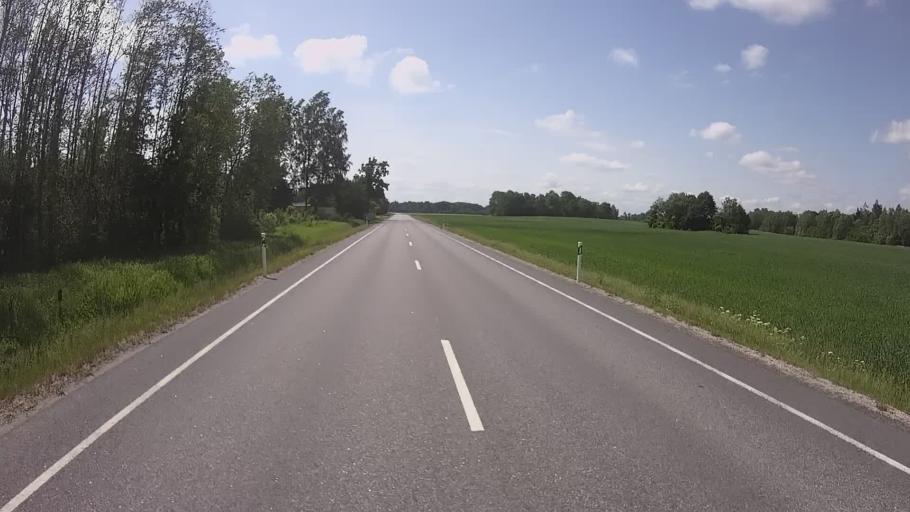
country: EE
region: Tartu
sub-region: Tartu linn
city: Tartu
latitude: 58.3829
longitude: 26.8873
